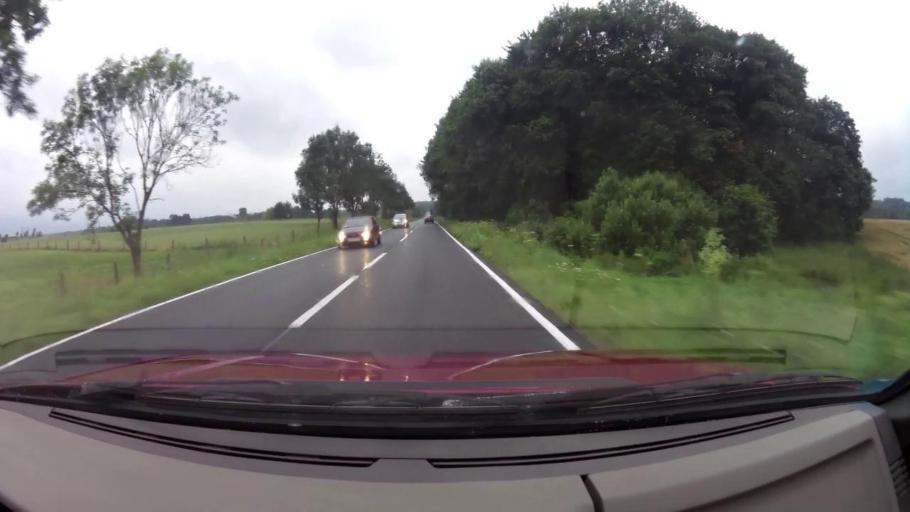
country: PL
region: West Pomeranian Voivodeship
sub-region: Powiat stargardzki
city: Marianowo
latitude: 53.4304
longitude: 15.2919
